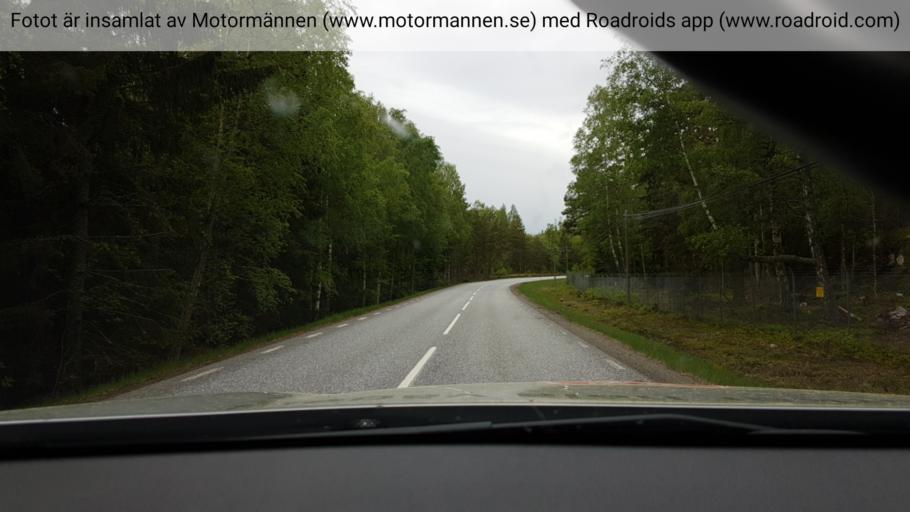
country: SE
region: Stockholm
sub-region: Nynashamns Kommun
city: Nynashamn
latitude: 58.9824
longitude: 18.0900
